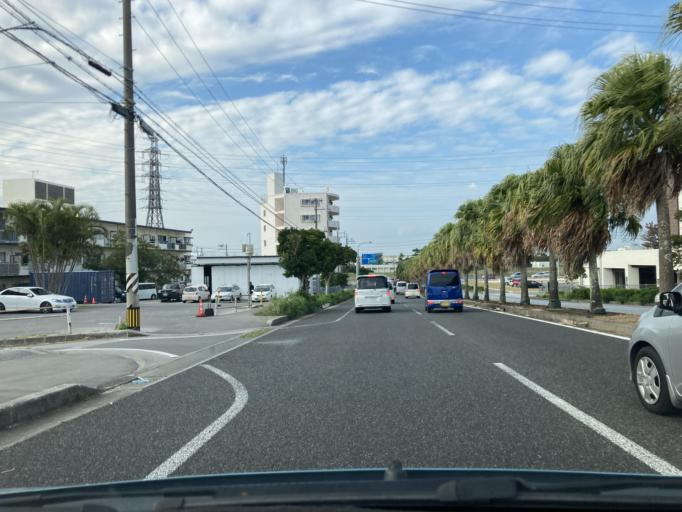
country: JP
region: Okinawa
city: Okinawa
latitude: 26.3318
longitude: 127.7832
